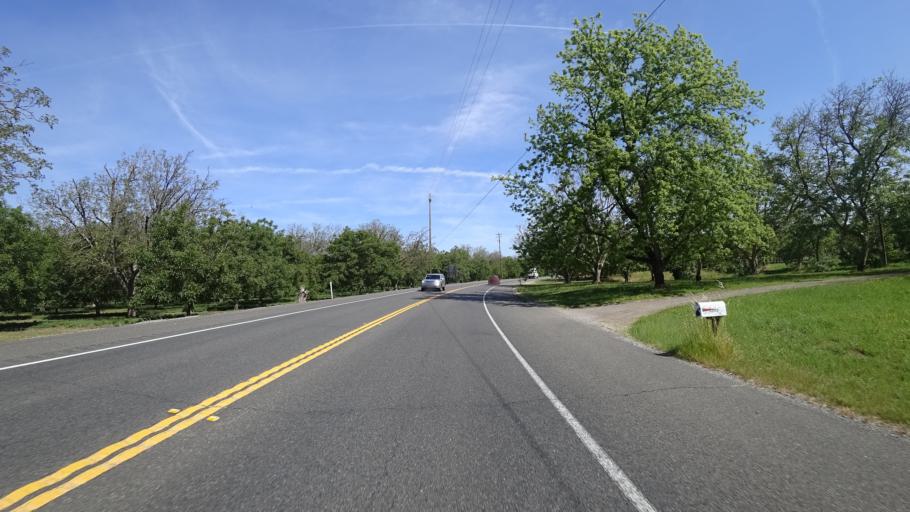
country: US
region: California
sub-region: Tehama County
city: Red Bluff
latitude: 40.1673
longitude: -122.1571
